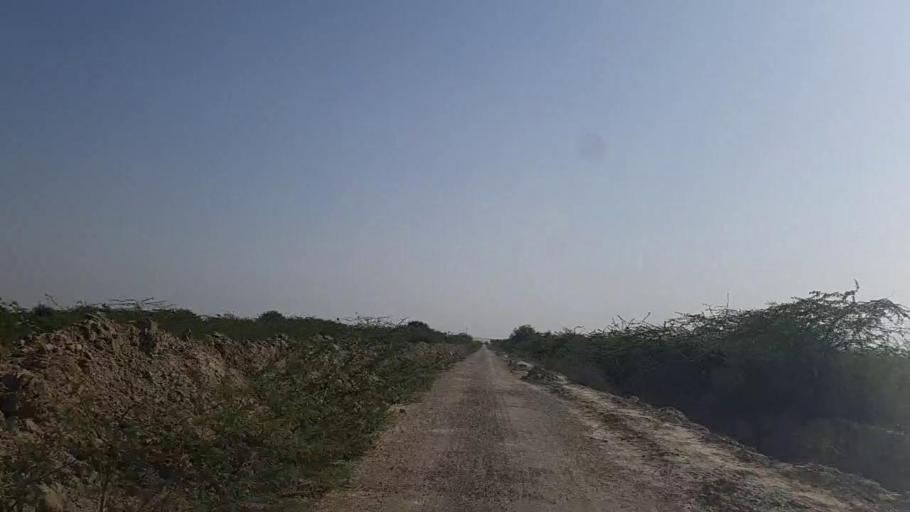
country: PK
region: Sindh
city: Kadhan
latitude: 24.5832
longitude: 69.2629
